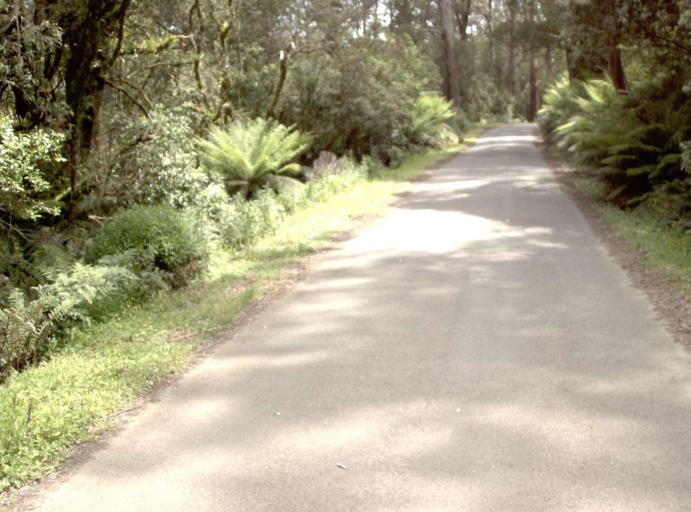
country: AU
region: Victoria
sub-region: Latrobe
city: Traralgon
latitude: -38.4213
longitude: 146.5752
